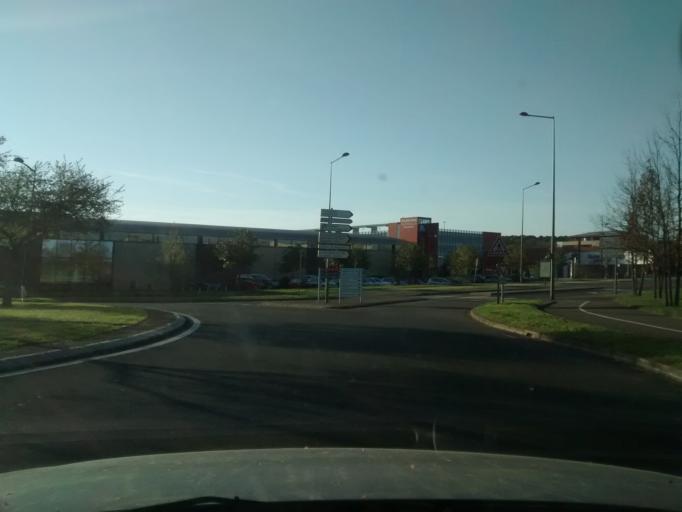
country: FR
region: Pays de la Loire
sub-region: Departement de la Sarthe
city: Rouillon
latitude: 48.0158
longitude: 0.1528
